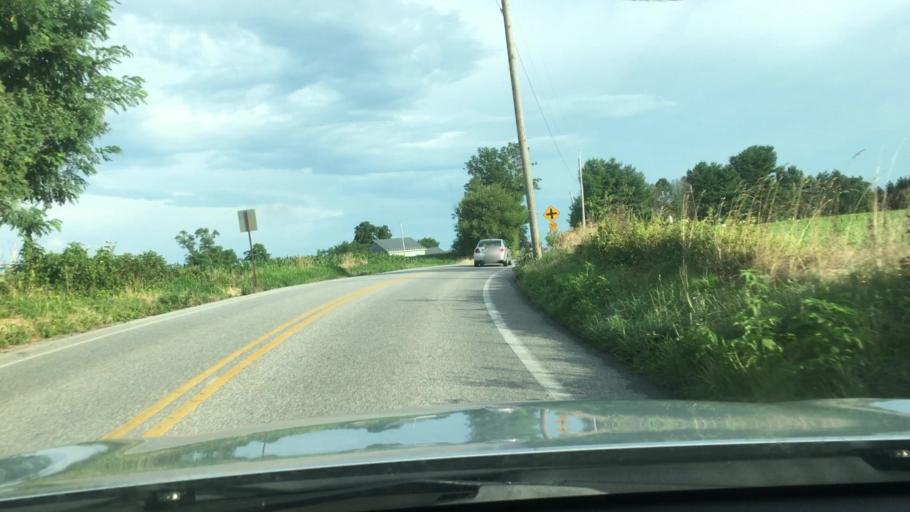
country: US
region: Pennsylvania
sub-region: York County
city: Shiloh
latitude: 40.0068
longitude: -76.8037
